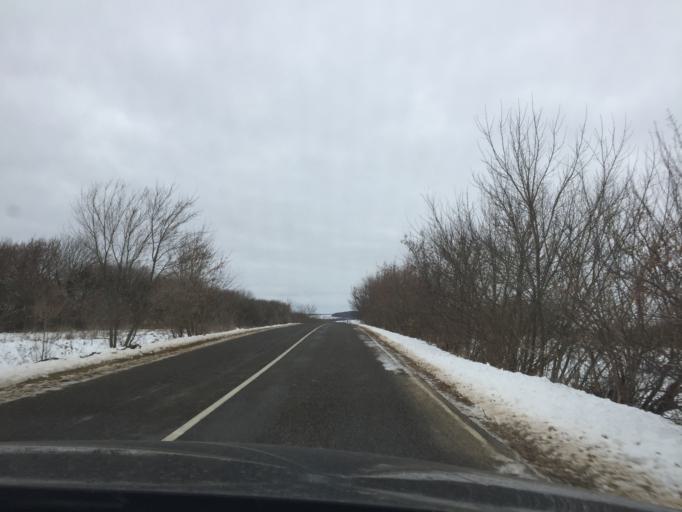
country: RU
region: Tula
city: Teploye
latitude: 53.7862
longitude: 37.6197
